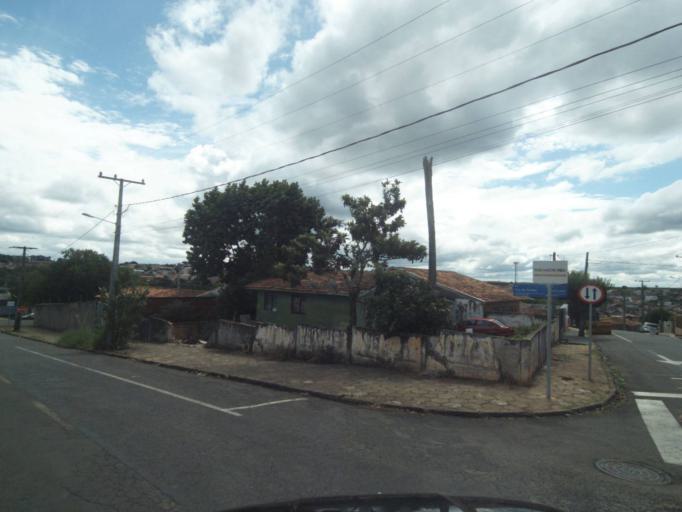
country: BR
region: Parana
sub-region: Telemaco Borba
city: Telemaco Borba
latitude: -24.3195
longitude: -50.6412
